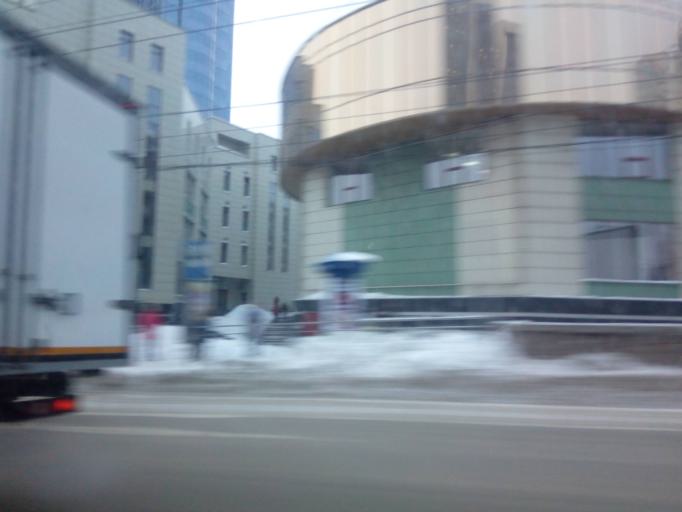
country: RU
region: Novosibirsk
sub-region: Novosibirskiy Rayon
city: Novosibirsk
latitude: 55.0285
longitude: 82.9065
